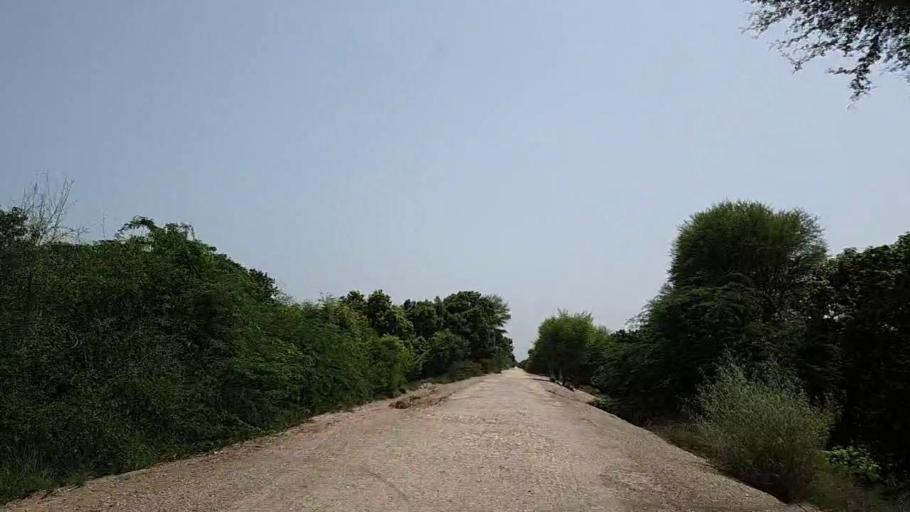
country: PK
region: Sindh
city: Kandiaro
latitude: 27.0380
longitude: 68.1275
